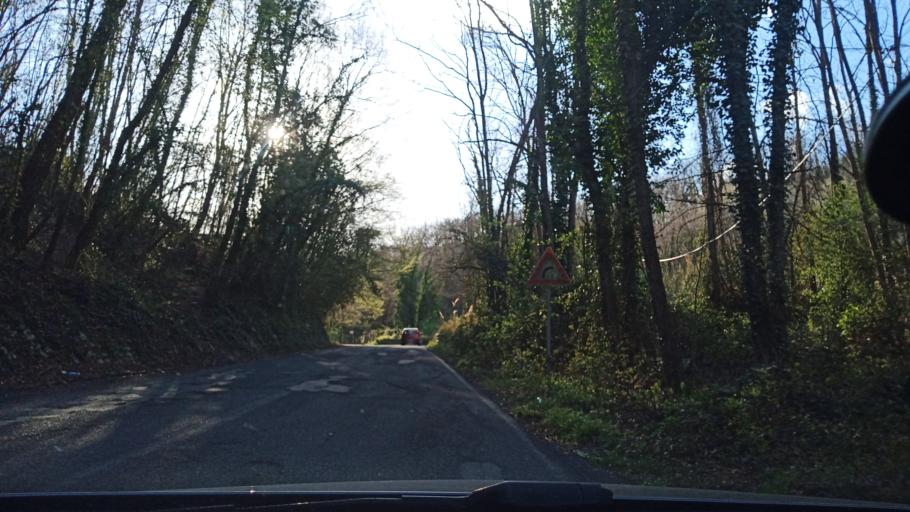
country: IT
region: Latium
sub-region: Citta metropolitana di Roma Capitale
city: Nazzano
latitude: 42.2108
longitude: 12.5998
